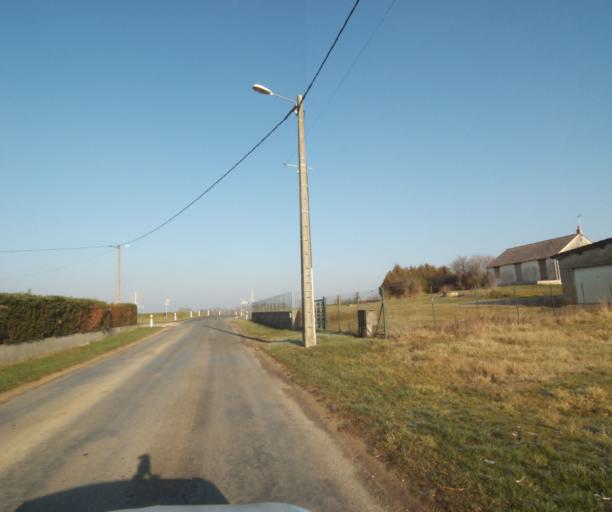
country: FR
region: Champagne-Ardenne
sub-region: Departement de la Haute-Marne
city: Montier-en-Der
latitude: 48.4138
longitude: 4.7416
